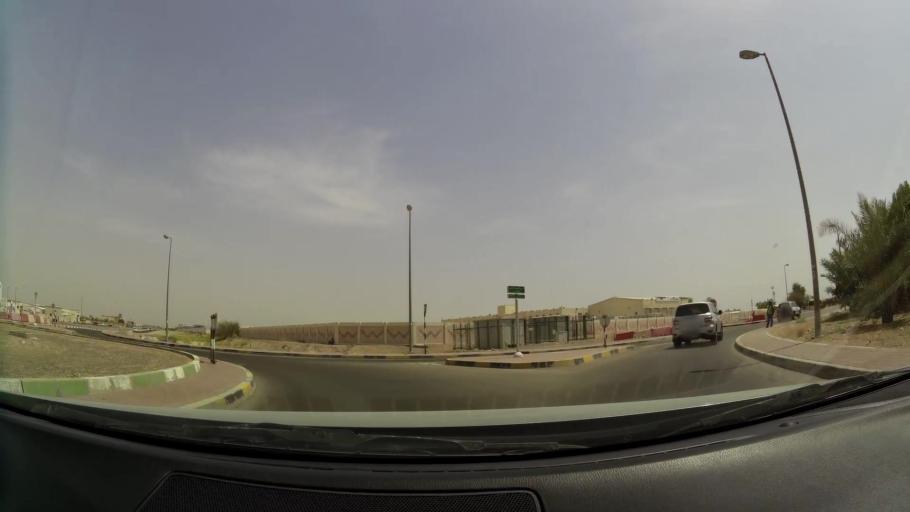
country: AE
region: Abu Dhabi
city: Al Ain
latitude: 24.1840
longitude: 55.7142
